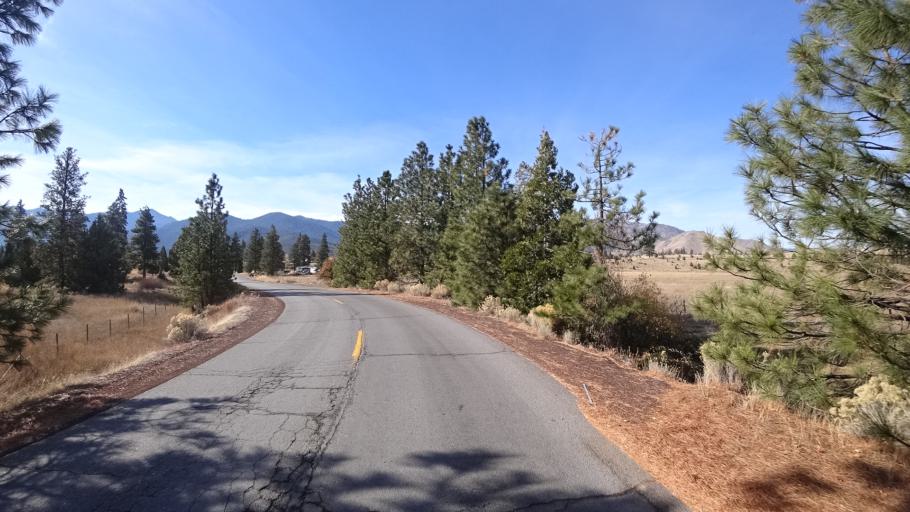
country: US
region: California
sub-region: Siskiyou County
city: Weed
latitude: 41.4474
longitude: -122.4323
